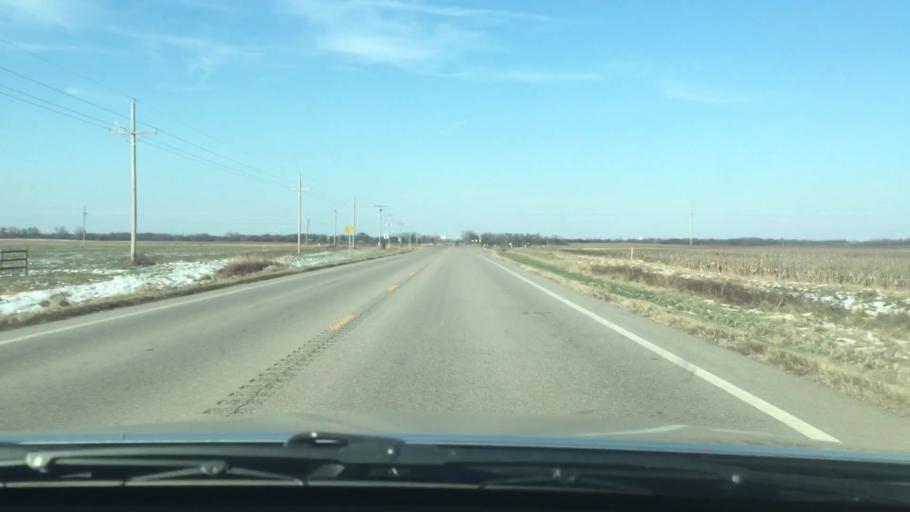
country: US
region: Kansas
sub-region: Rice County
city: Lyons
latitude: 38.2875
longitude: -98.2019
